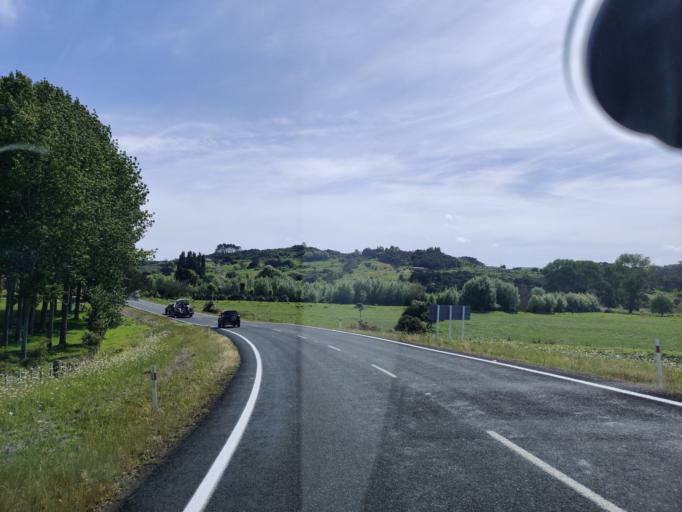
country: NZ
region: Northland
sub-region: Far North District
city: Kaitaia
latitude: -35.4597
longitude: 173.4662
